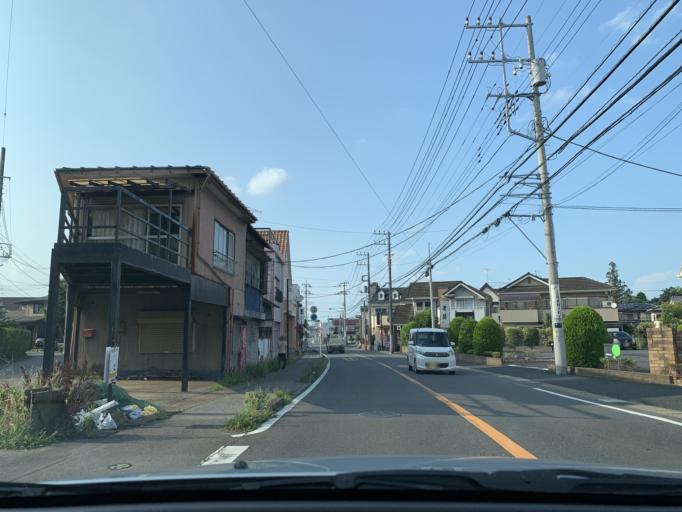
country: JP
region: Chiba
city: Kashiwa
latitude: 35.8692
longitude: 139.9402
